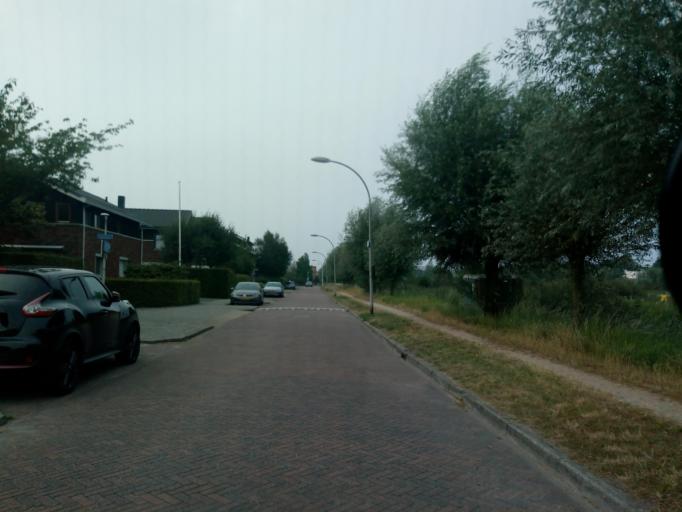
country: NL
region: South Holland
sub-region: Gemeente Alphen aan den Rijn
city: Alphen aan den Rijn
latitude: 52.1151
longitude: 4.6538
